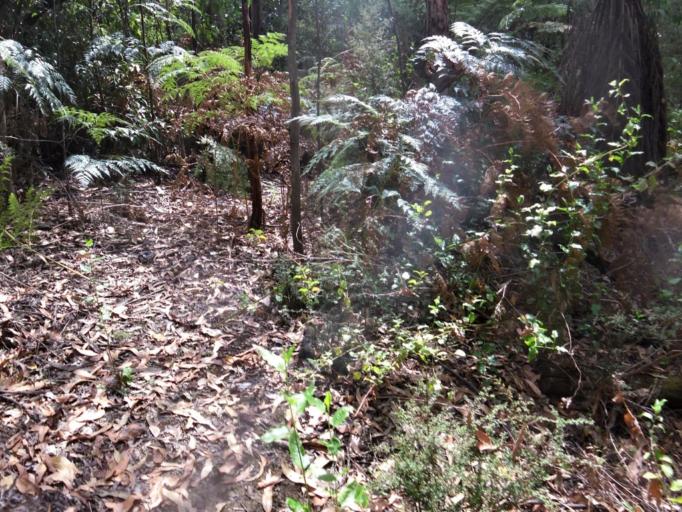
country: AU
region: Victoria
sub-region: Nillumbik
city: Saint Andrews
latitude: -37.5389
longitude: 145.3474
